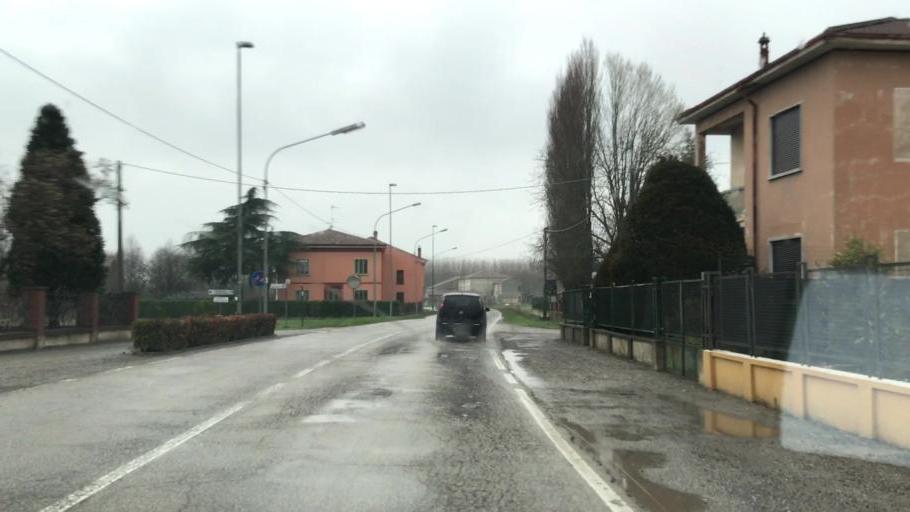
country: IT
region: Lombardy
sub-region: Provincia di Mantova
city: Borgofranco sul Po
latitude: 45.0495
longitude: 11.2041
